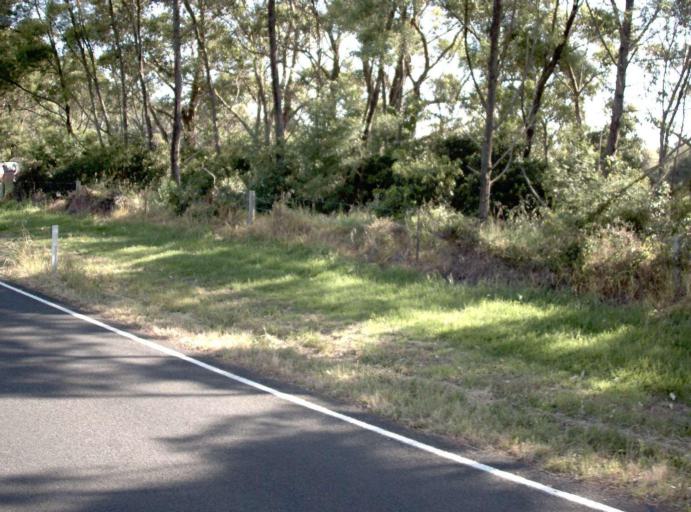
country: AU
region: Victoria
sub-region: East Gippsland
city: Lakes Entrance
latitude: -37.7477
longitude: 148.5171
